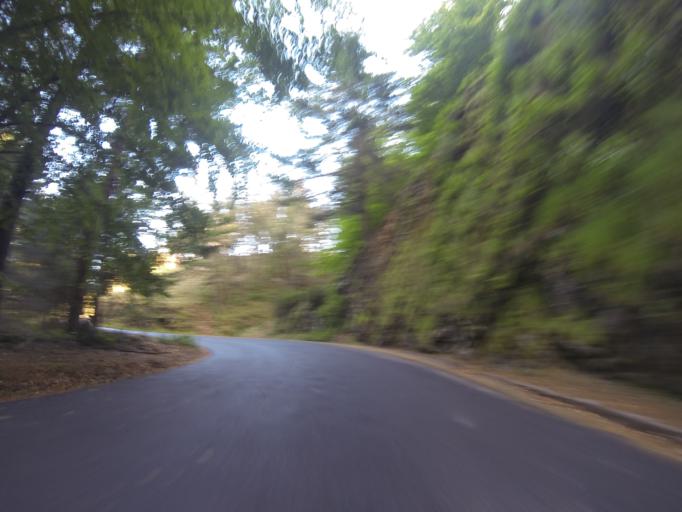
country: PT
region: Madeira
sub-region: Funchal
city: Nossa Senhora do Monte
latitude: 32.6958
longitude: -16.8780
